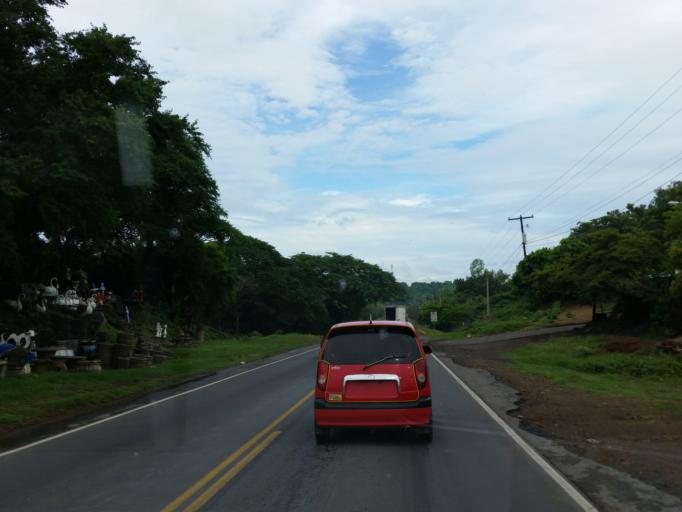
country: NI
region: Managua
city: Ciudad Sandino
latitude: 12.2397
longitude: -86.4372
